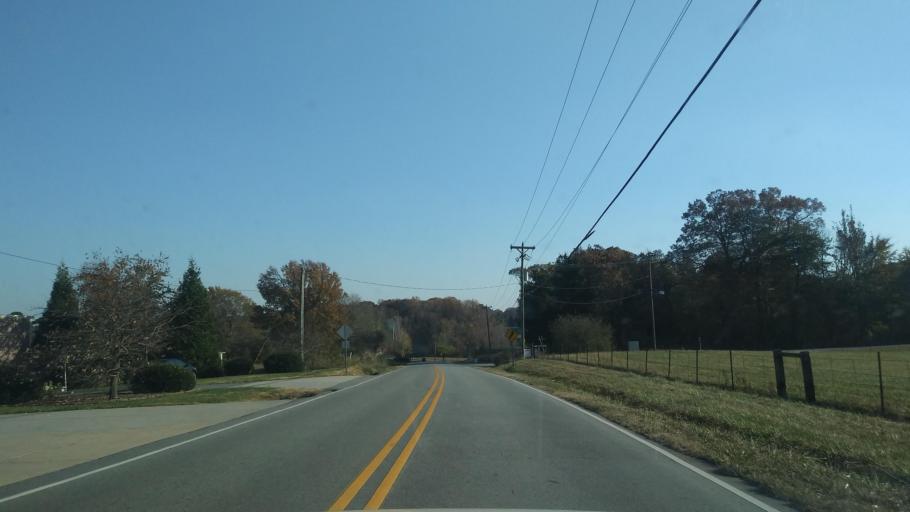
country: US
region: North Carolina
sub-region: Guilford County
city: McLeansville
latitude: 36.2090
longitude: -79.7148
